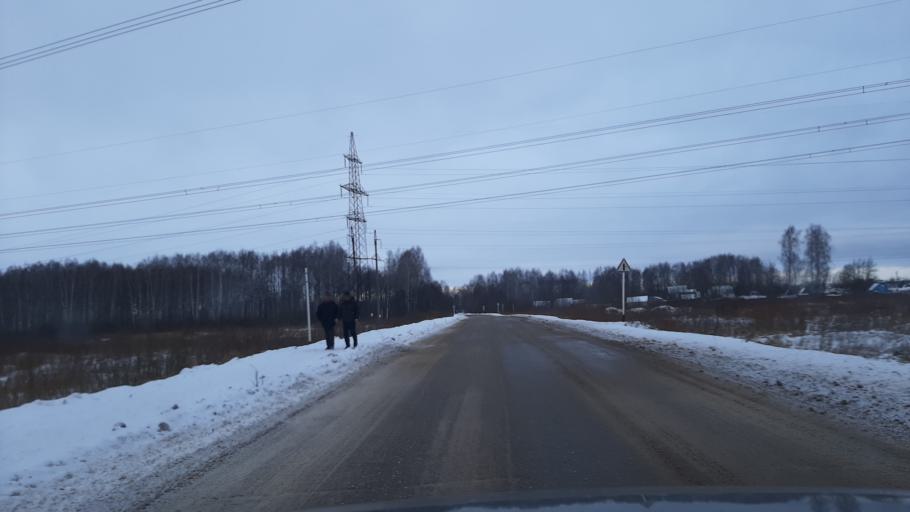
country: RU
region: Kostroma
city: Volgorechensk
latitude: 57.4444
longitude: 41.1397
